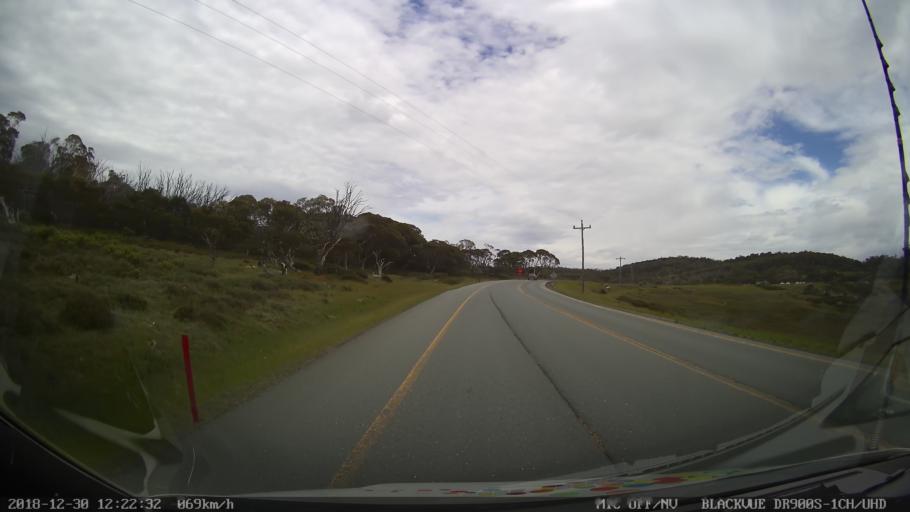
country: AU
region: New South Wales
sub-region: Snowy River
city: Jindabyne
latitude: -36.3600
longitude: 148.5095
